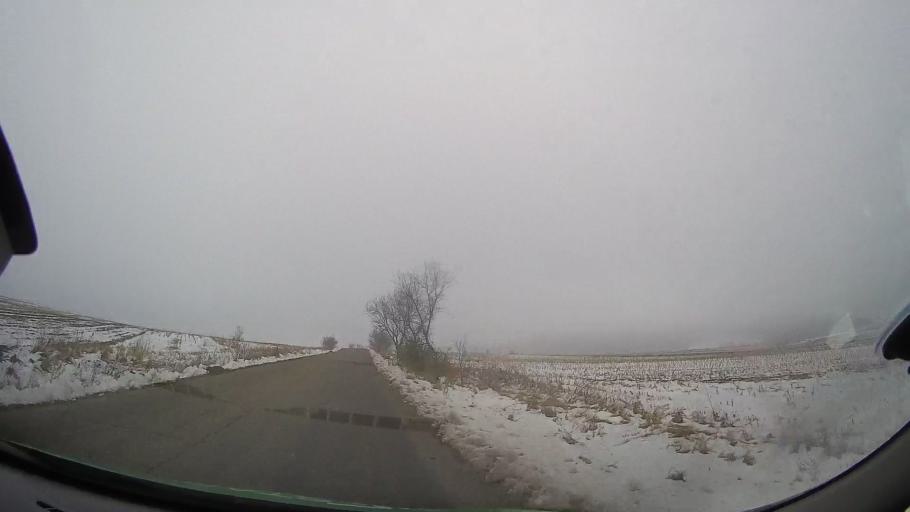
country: RO
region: Bacau
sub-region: Comuna Glavanesti
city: Frumuselu
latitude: 46.2688
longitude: 27.3094
